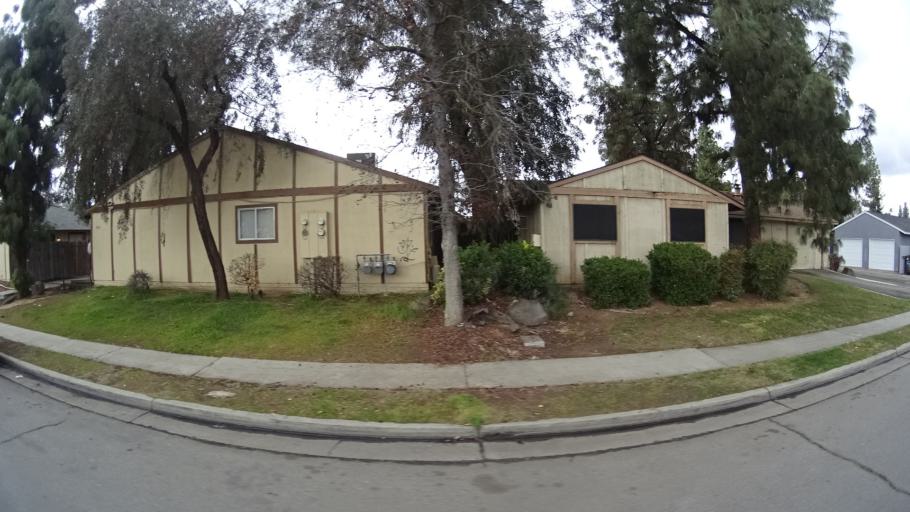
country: US
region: California
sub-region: Fresno County
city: West Park
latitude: 36.7882
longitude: -119.8444
